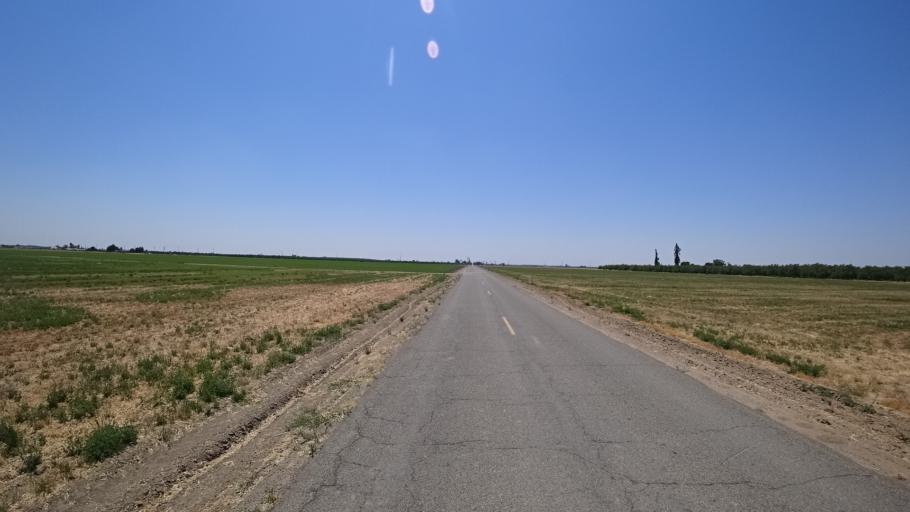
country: US
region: California
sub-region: Kings County
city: Lucerne
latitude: 36.3762
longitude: -119.7270
